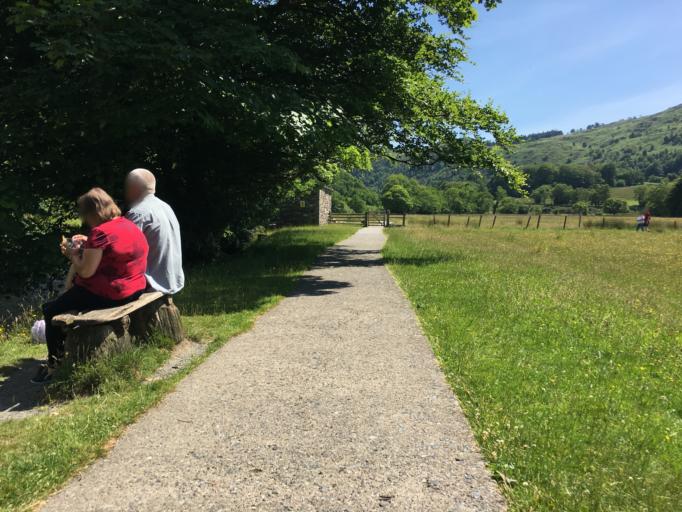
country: GB
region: Wales
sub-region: Gwynedd
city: Penrhyndeudraeth
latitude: 53.0092
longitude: -4.1007
